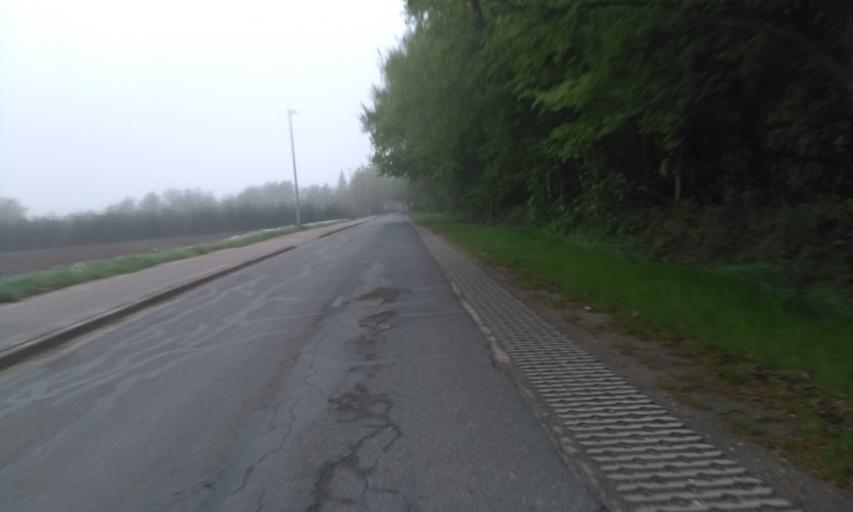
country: DE
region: Lower Saxony
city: Nottensdorf
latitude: 53.4729
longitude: 9.6163
